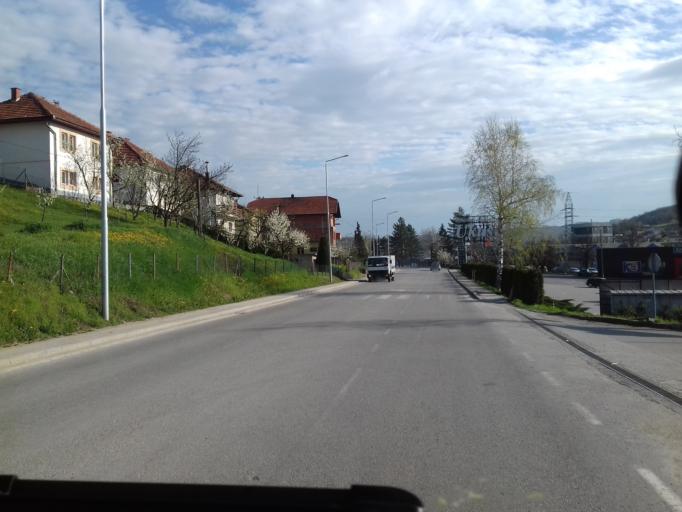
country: BA
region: Federation of Bosnia and Herzegovina
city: Tesanj
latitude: 44.6239
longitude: 17.9983
